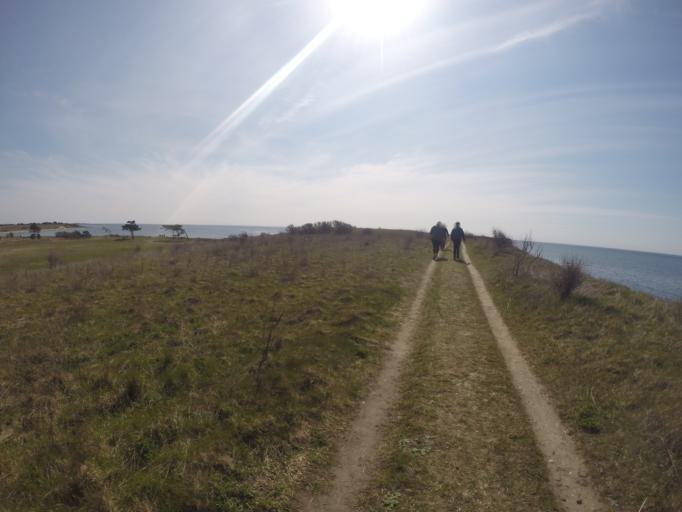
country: DK
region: Zealand
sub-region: Kalundborg Kommune
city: Gorlev
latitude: 55.5162
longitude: 11.0814
